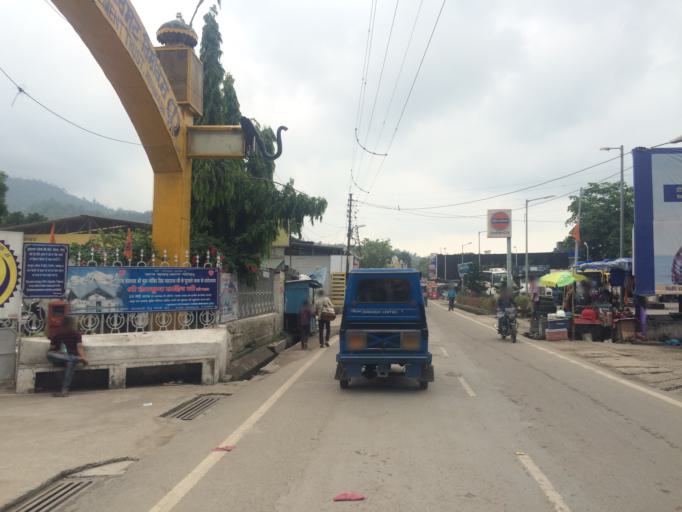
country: IN
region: Uttarakhand
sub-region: Dehradun
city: Rishikesh
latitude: 30.1126
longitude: 78.3029
